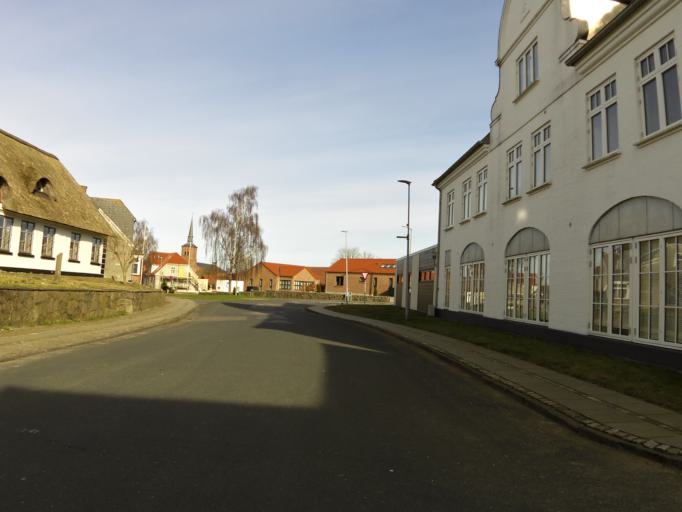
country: DK
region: South Denmark
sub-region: Kolding Kommune
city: Vamdrup
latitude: 55.3563
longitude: 9.1982
